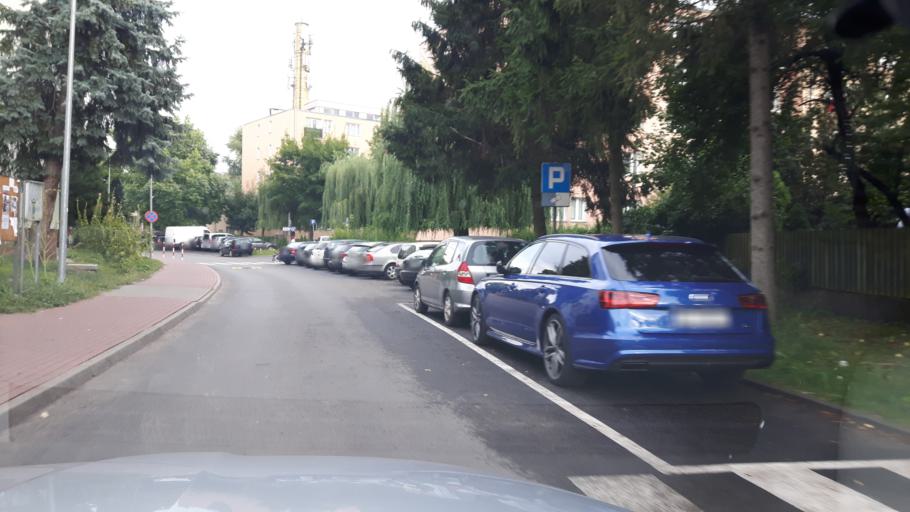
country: PL
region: Masovian Voivodeship
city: Zielonka
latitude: 52.3149
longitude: 21.1598
